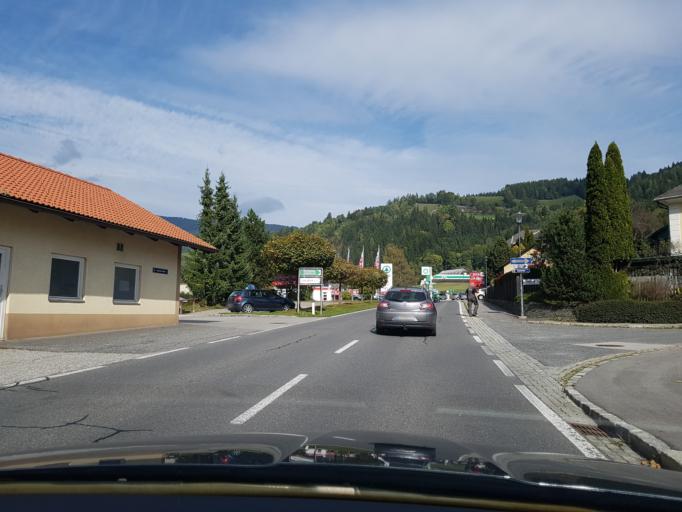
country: AT
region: Carinthia
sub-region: Politischer Bezirk Feldkirchen
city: Himmelberg
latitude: 46.7506
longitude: 14.0344
